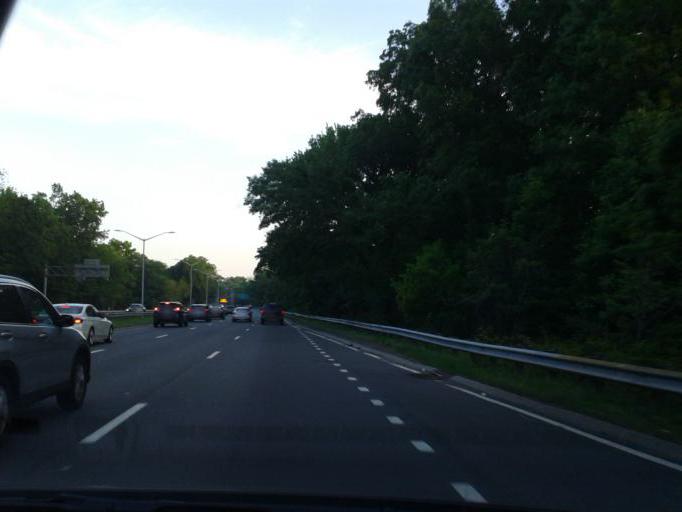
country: US
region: New York
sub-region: Bronx
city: The Bronx
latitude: 40.8748
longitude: -73.8714
